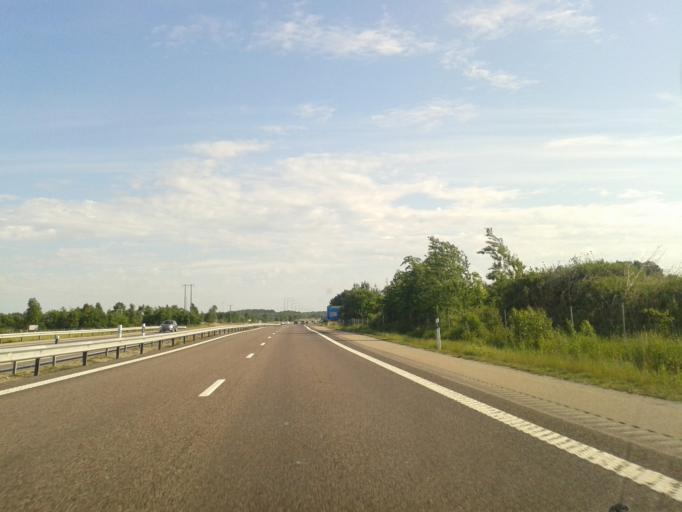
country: SE
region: Vaestra Goetaland
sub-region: Stenungsunds Kommun
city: Stora Hoga
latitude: 58.0135
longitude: 11.8435
